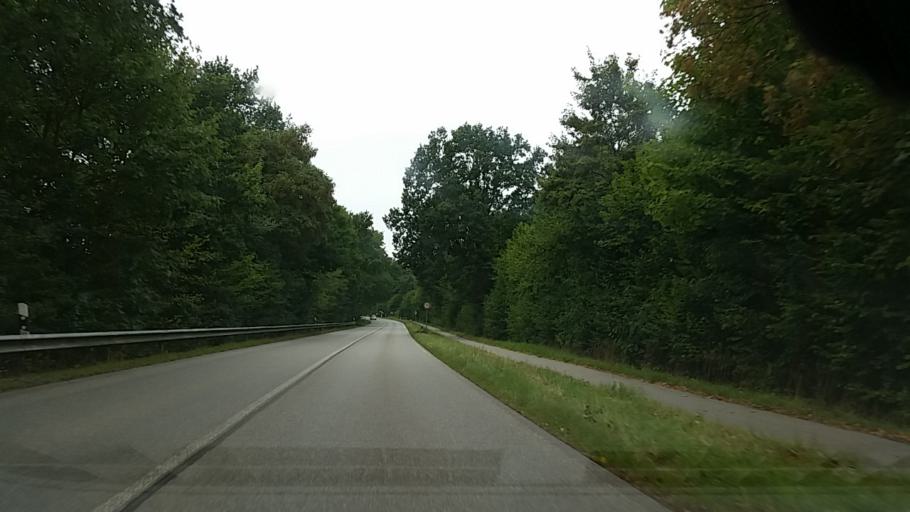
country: DE
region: Schleswig-Holstein
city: Wohltorf
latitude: 53.5295
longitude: 10.2757
